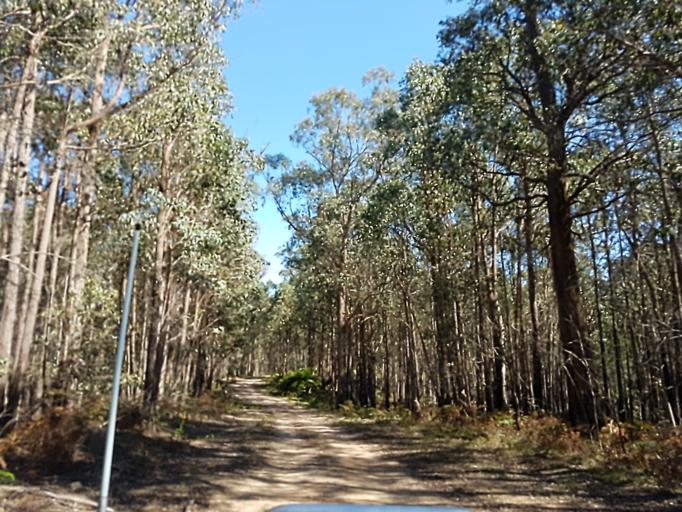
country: AU
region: Victoria
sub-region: East Gippsland
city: Lakes Entrance
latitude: -37.2320
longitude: 148.2881
